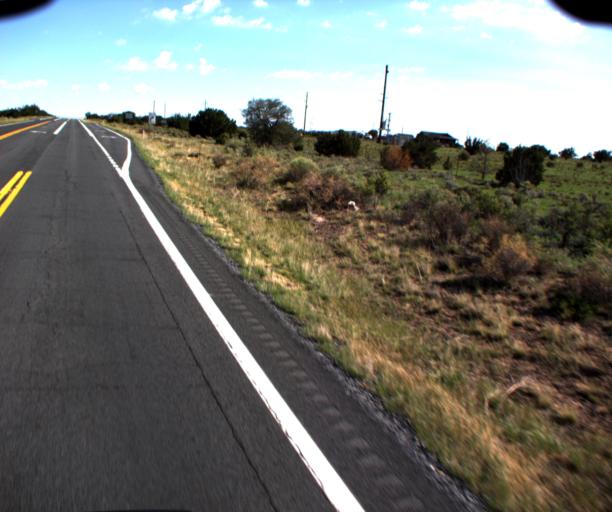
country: US
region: Arizona
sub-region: Coconino County
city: Williams
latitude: 35.5010
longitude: -112.1739
